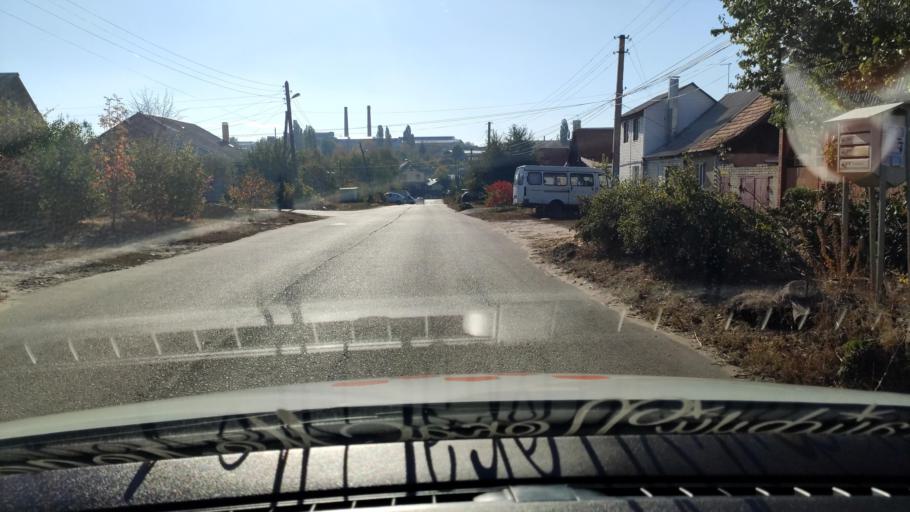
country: RU
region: Voronezj
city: Voronezh
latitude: 51.6961
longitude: 39.1691
